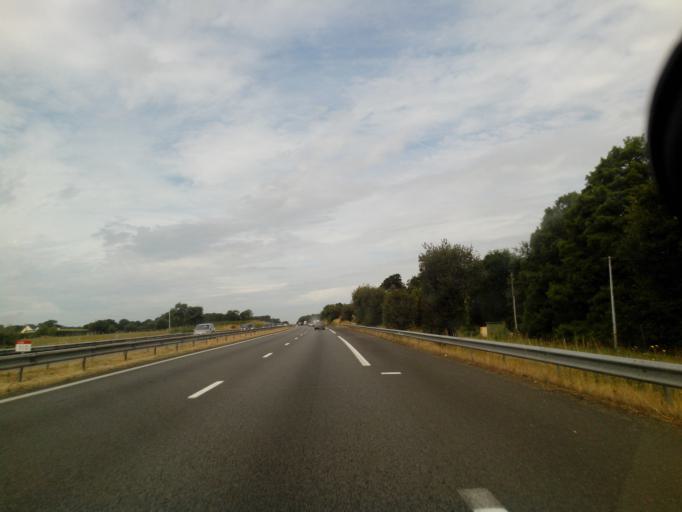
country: FR
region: Brittany
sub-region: Departement du Morbihan
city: Ploeren
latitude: 47.6613
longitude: -2.8296
